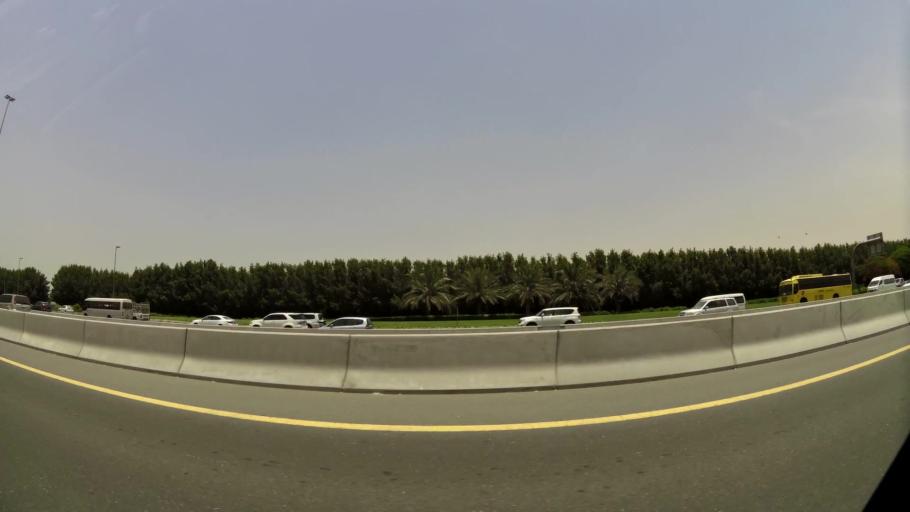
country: AE
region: Ash Shariqah
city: Sharjah
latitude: 25.2212
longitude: 55.3689
